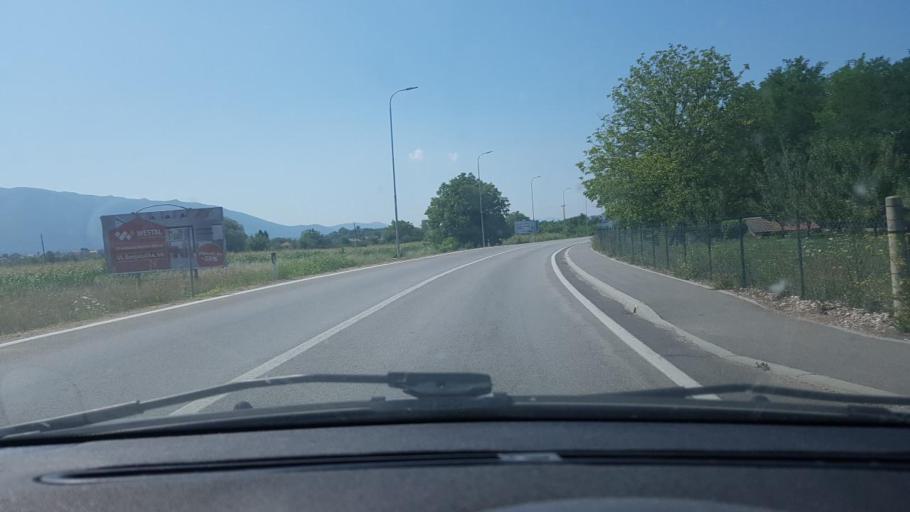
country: BA
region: Federation of Bosnia and Herzegovina
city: Bihac
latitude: 44.8078
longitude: 15.8859
